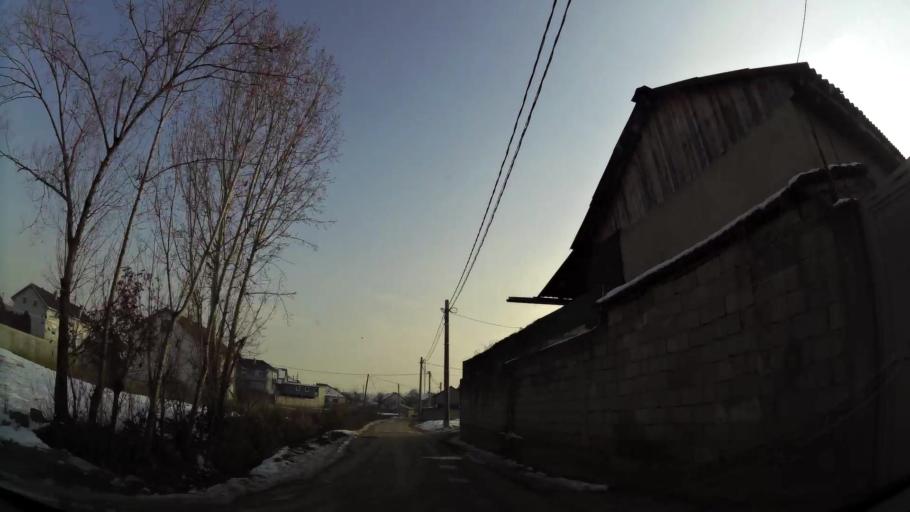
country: MK
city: Creshevo
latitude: 42.0230
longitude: 21.5004
